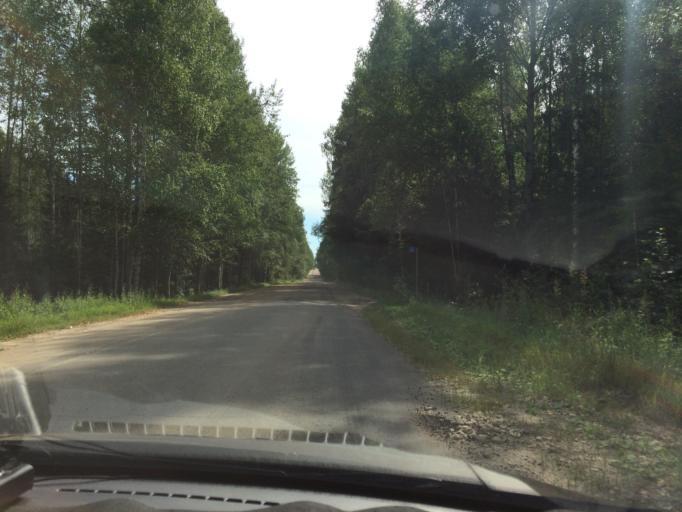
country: RU
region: Mariy-El
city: Mochalishche
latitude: 56.5470
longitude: 48.3614
